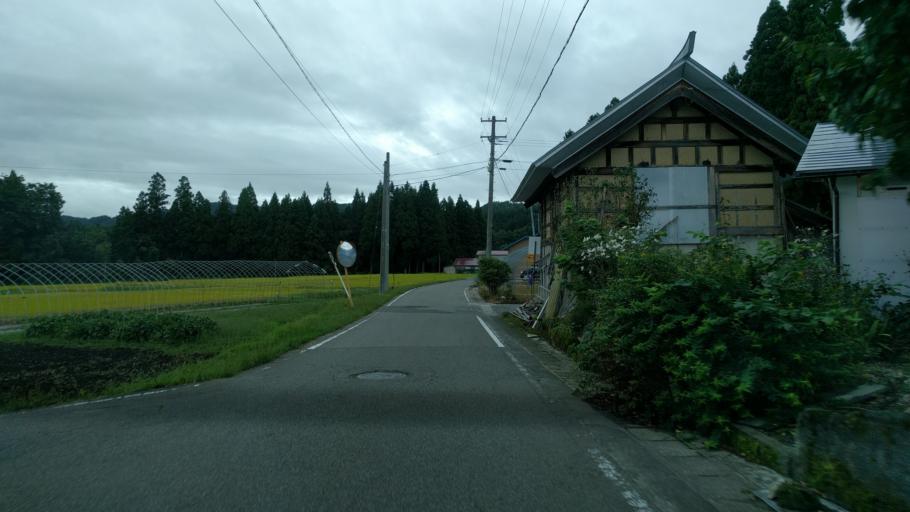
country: JP
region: Fukushima
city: Kitakata
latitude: 37.5426
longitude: 139.7314
